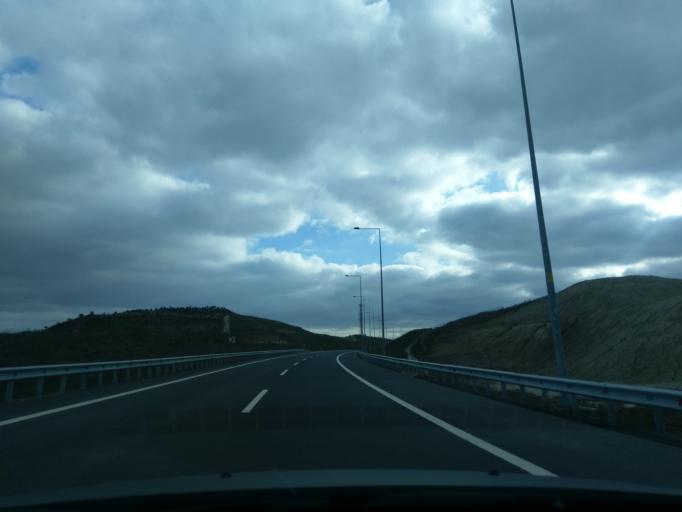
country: TR
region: Istanbul
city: Kemerburgaz
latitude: 41.2348
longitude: 28.8389
